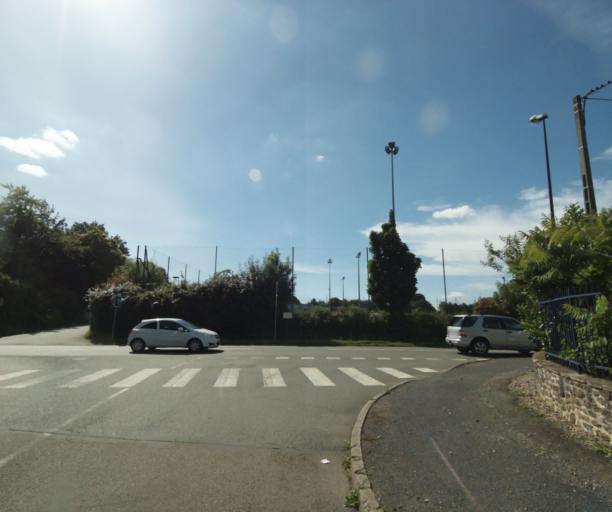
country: FR
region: Pays de la Loire
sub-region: Departement de la Mayenne
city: Change
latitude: 48.0707
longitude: -0.8009
